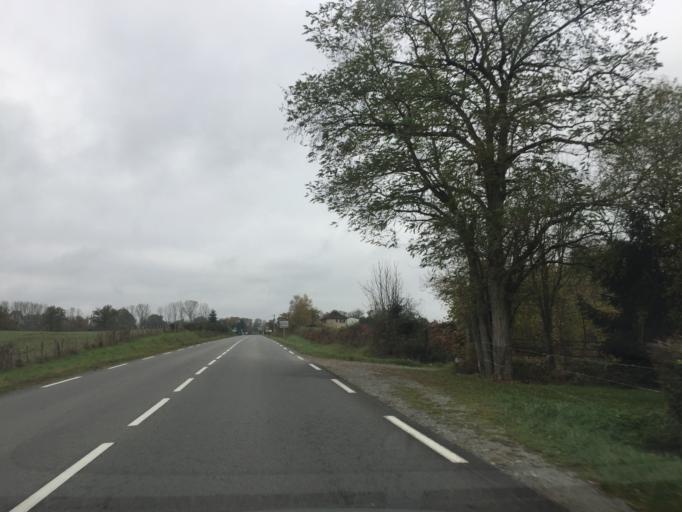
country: FR
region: Limousin
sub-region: Departement de la Creuse
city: Gouzon
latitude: 46.1219
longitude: 2.1842
